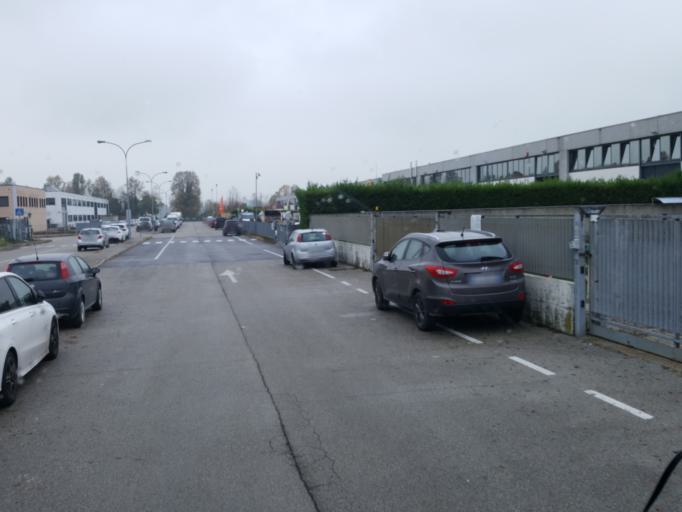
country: IT
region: Veneto
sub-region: Provincia di Treviso
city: Mogliano Veneto
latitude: 45.5533
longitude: 12.2267
